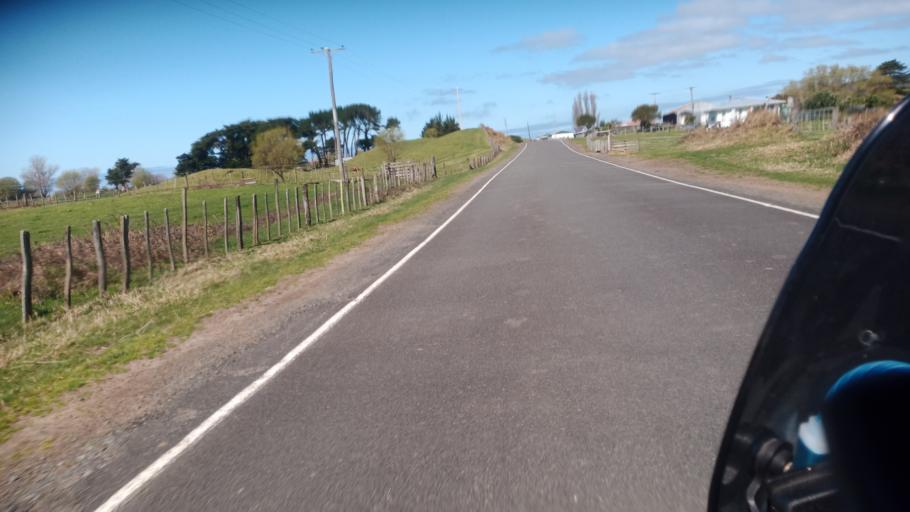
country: NZ
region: Gisborne
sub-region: Gisborne District
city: Gisborne
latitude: -39.0485
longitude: 177.8680
